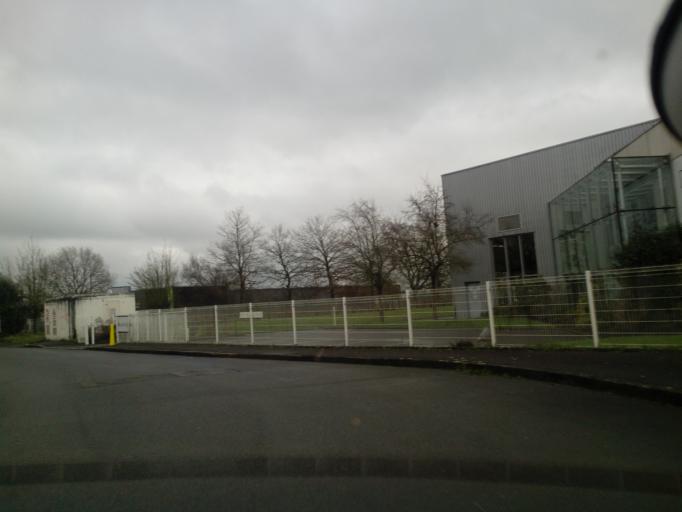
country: FR
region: Brittany
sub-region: Departement d'Ille-et-Vilaine
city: Vezin-le-Coquet
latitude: 48.1039
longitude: -1.7405
